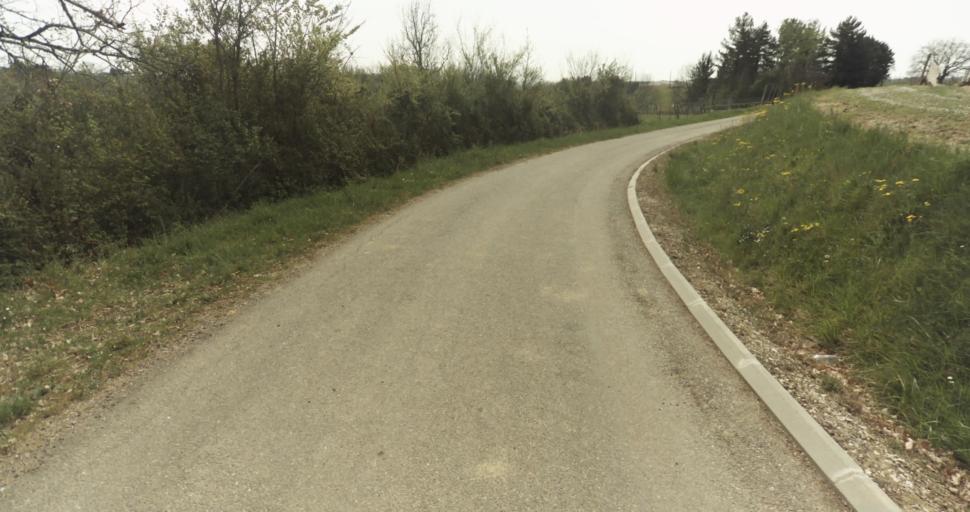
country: FR
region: Midi-Pyrenees
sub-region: Departement du Tarn-et-Garonne
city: Moissac
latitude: 44.1172
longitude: 1.0550
